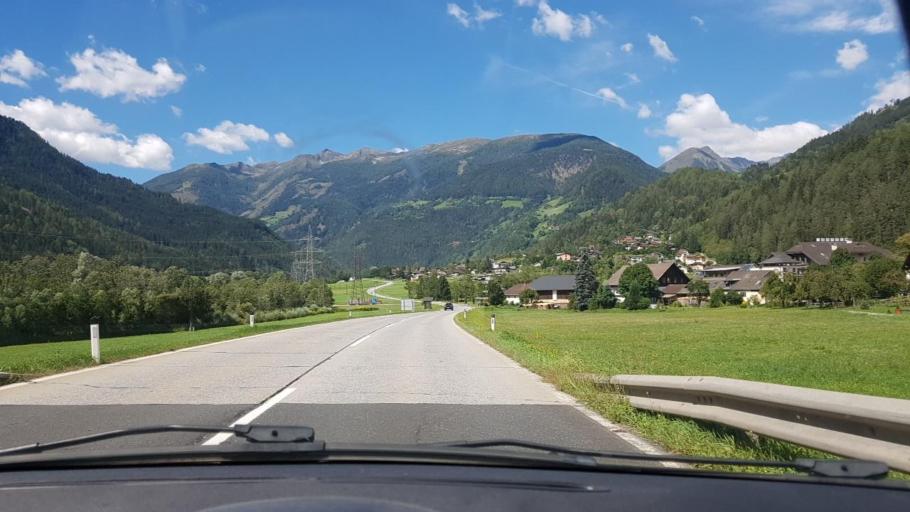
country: AT
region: Carinthia
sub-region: Politischer Bezirk Spittal an der Drau
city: Flattach
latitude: 46.9336
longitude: 13.1330
